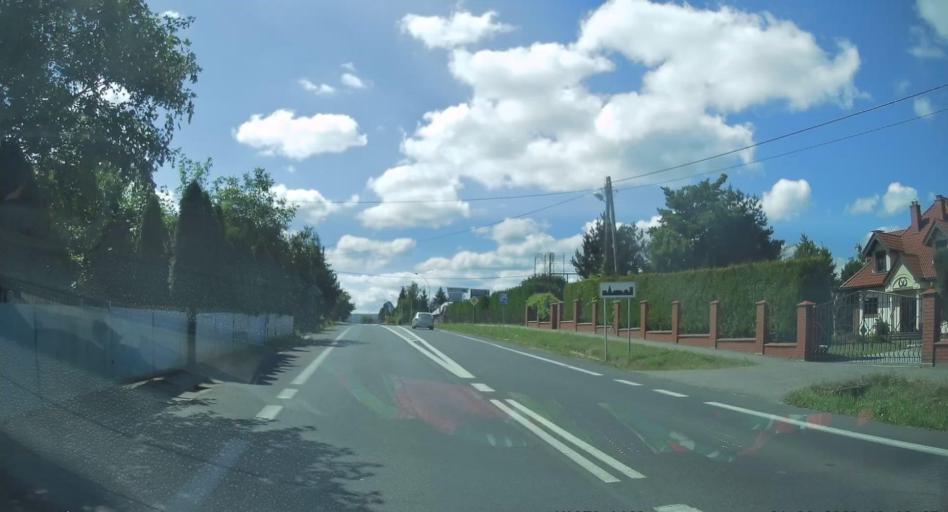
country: PL
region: Subcarpathian Voivodeship
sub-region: Powiat debicki
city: Brzeznica
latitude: 50.0742
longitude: 21.4505
